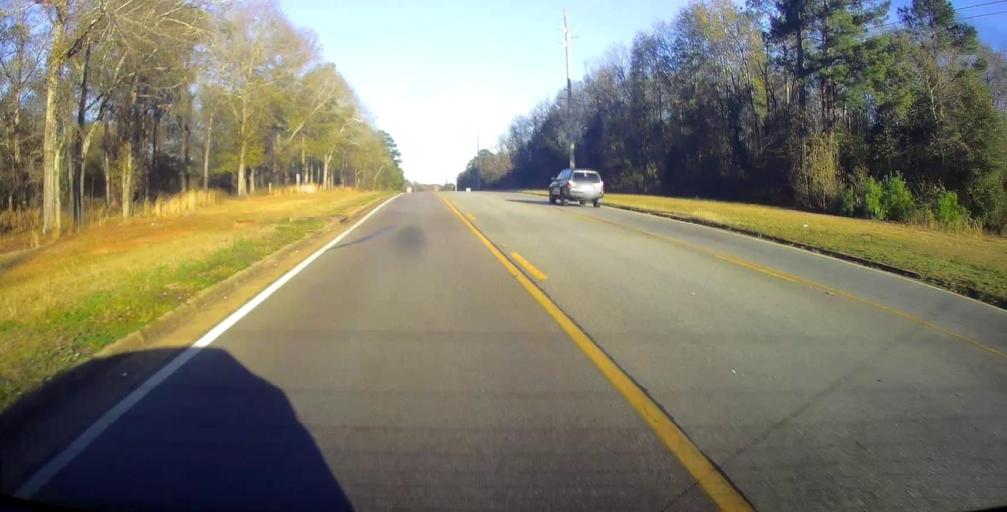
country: US
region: Georgia
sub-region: Dougherty County
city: Albany
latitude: 31.6229
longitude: -84.1840
